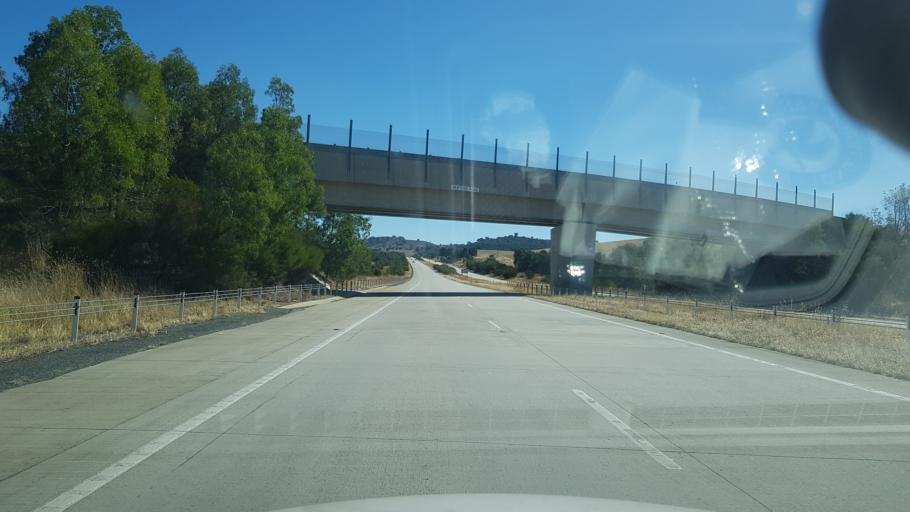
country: AU
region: New South Wales
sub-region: Albury Municipality
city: Lavington
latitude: -35.9157
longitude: 147.1254
